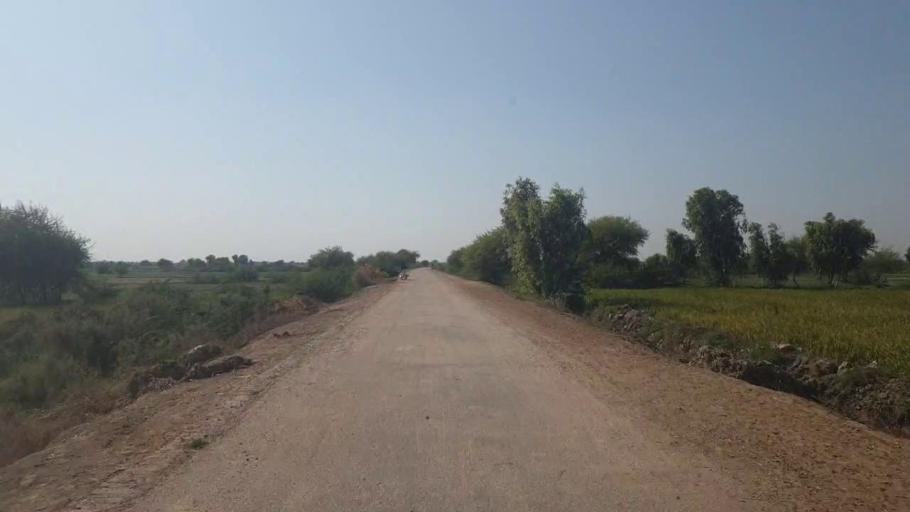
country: PK
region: Sindh
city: Badin
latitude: 24.5545
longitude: 68.8268
